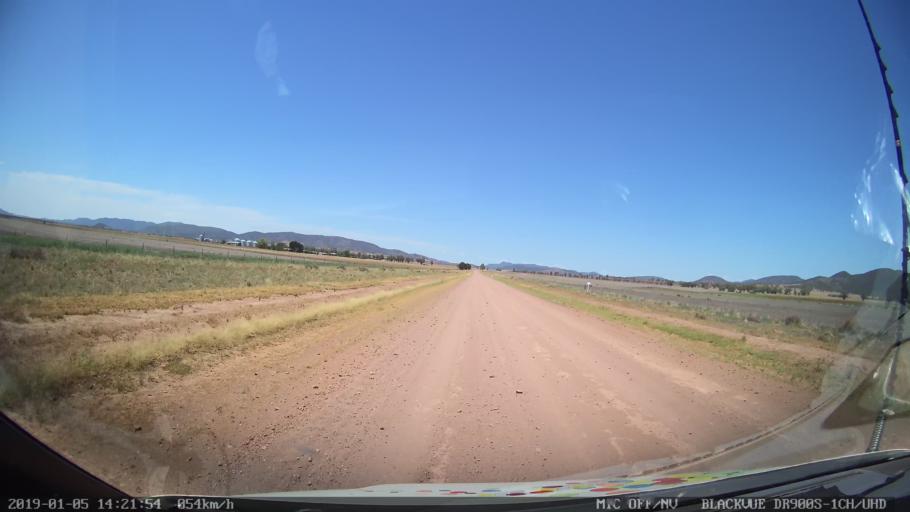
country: AU
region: New South Wales
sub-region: Liverpool Plains
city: Quirindi
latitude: -31.2456
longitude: 150.5173
